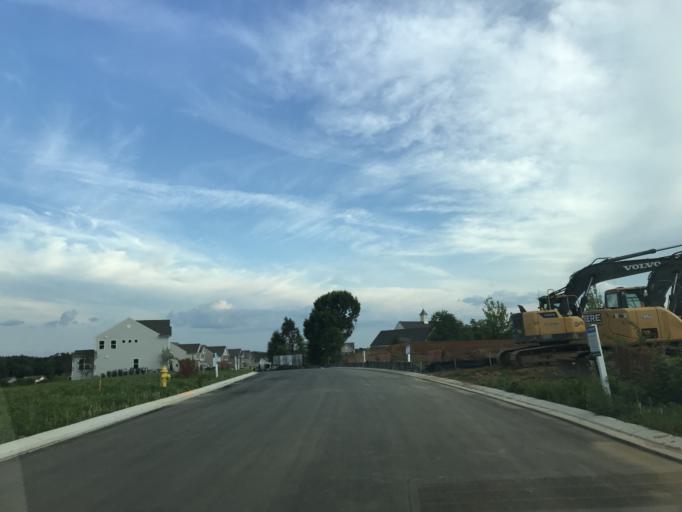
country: US
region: Maryland
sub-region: Harford County
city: Perryman
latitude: 39.5019
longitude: -76.2070
